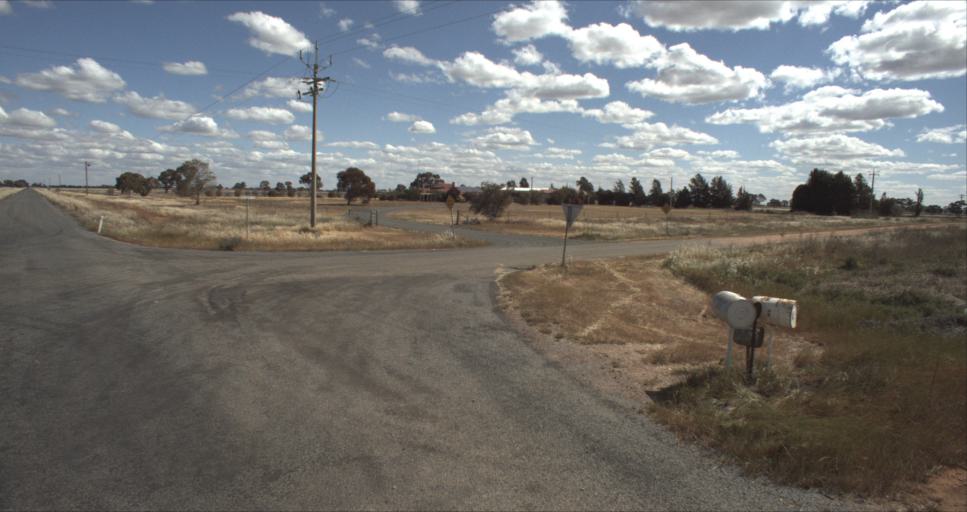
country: AU
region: New South Wales
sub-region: Leeton
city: Leeton
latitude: -34.4591
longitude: 146.2531
